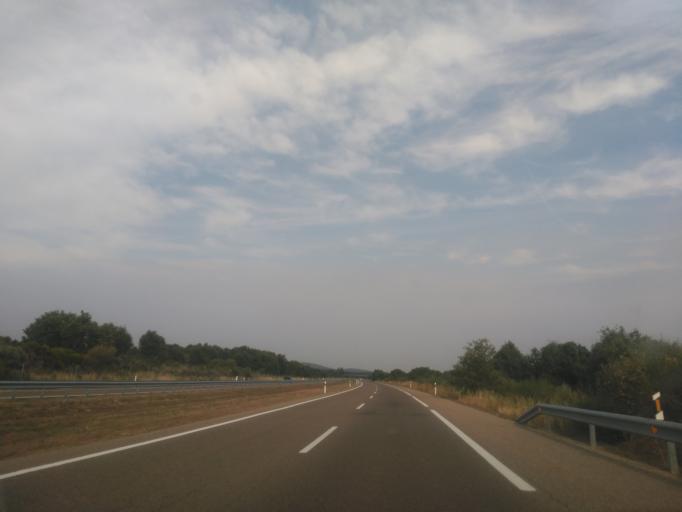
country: ES
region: Castille and Leon
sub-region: Provincia de Zamora
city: Asturianos
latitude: 42.0395
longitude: -6.4578
